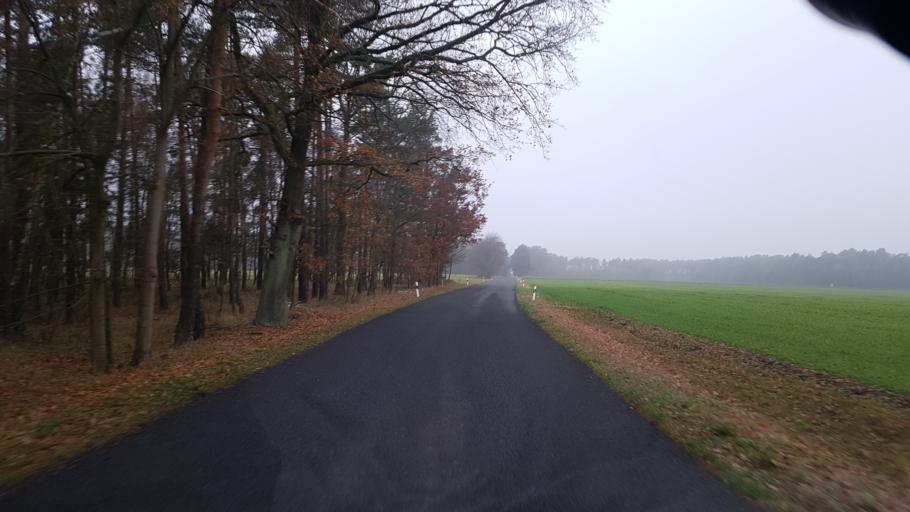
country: DE
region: Brandenburg
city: Bronkow
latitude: 51.6864
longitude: 13.9420
